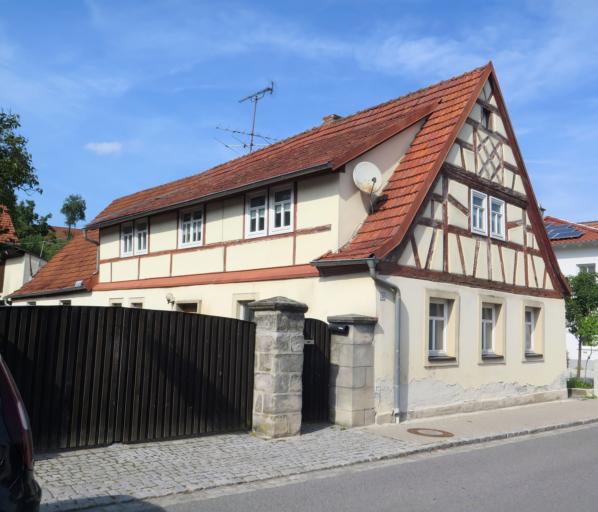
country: DE
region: Bavaria
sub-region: Regierungsbezirk Unterfranken
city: Sand
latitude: 49.9424
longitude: 10.6048
